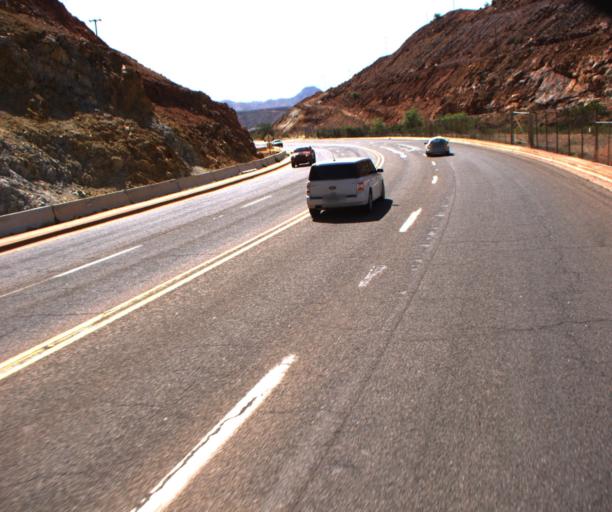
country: US
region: Arizona
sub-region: Cochise County
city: Bisbee
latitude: 31.4382
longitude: -109.9073
